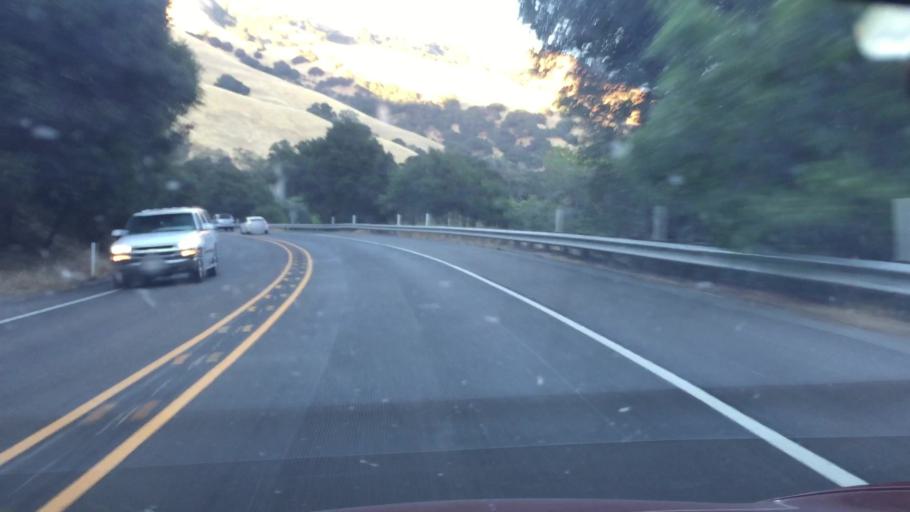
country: US
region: California
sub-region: Alameda County
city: Fremont
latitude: 37.5968
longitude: -121.9285
